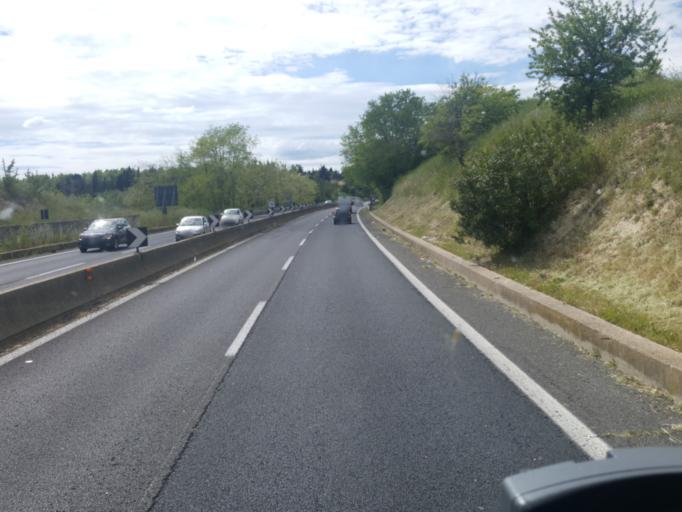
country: IT
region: Latium
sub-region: Citta metropolitana di Roma Capitale
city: La Massimina-Casal Lumbroso
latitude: 41.8856
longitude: 12.3208
